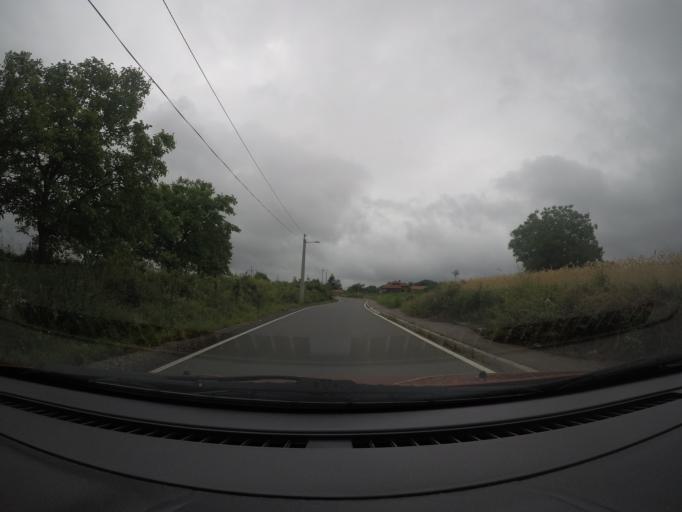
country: RS
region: Central Serbia
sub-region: Belgrade
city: Zvezdara
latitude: 44.7013
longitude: 20.5620
